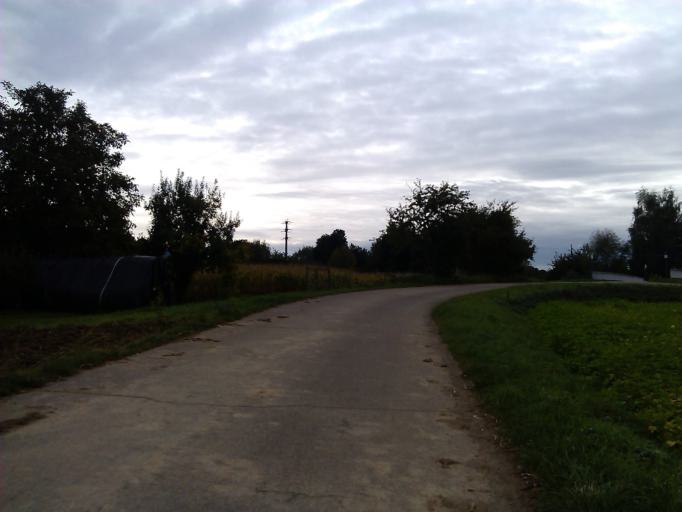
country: DE
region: Baden-Wuerttemberg
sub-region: Karlsruhe Region
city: Weinheim
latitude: 49.5658
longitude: 8.6494
